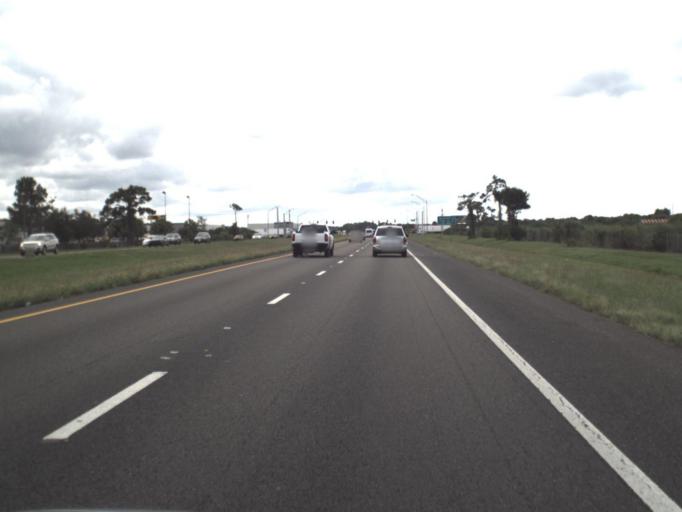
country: US
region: Florida
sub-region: Manatee County
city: Whitfield
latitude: 27.4076
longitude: -82.5331
